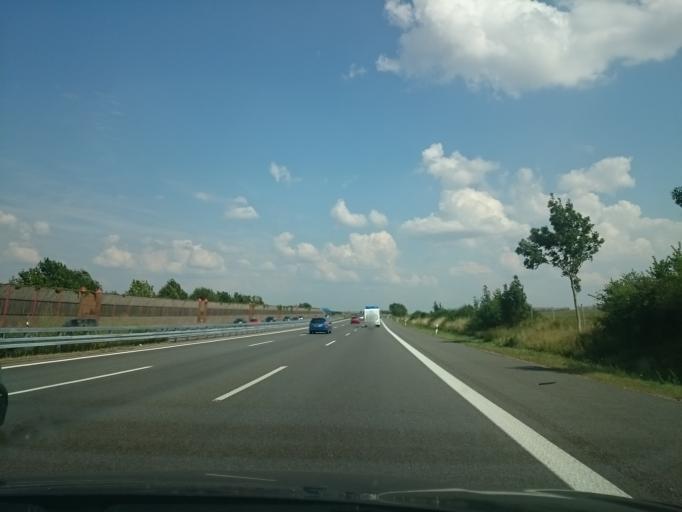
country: DE
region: Saxony
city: Reinsberg
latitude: 51.0488
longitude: 13.3483
